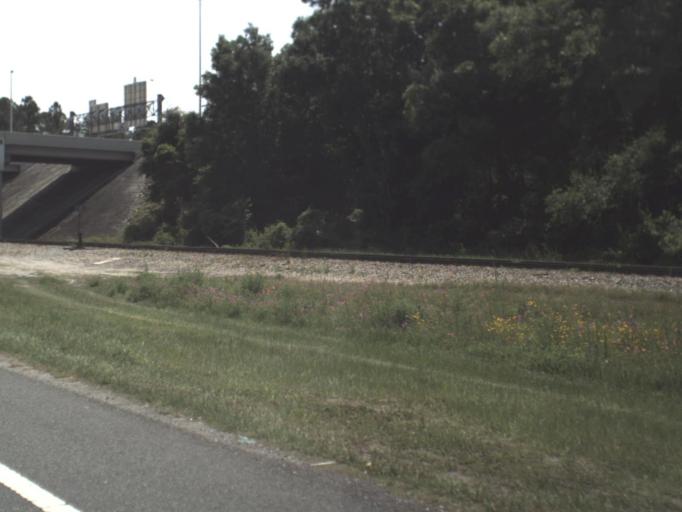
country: US
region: Florida
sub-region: Duval County
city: Jacksonville
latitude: 30.4583
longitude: -81.6357
